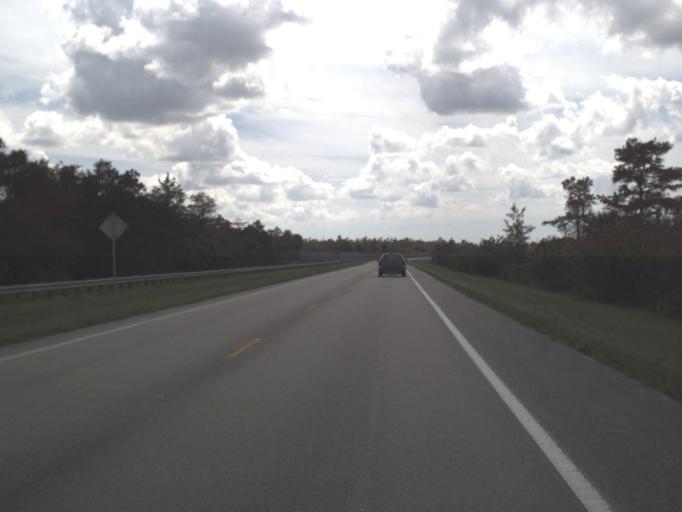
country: US
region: Florida
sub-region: Collier County
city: Lely Resort
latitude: 25.9906
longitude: -81.3475
